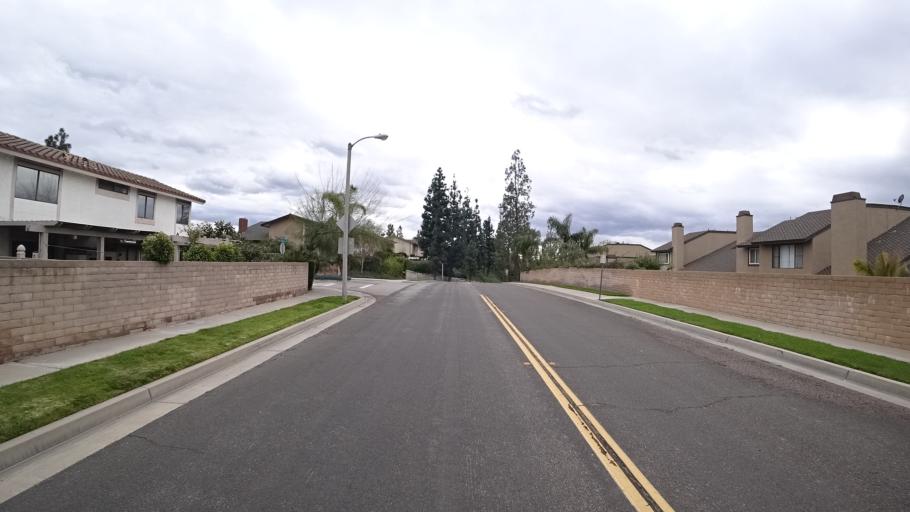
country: US
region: California
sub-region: Orange County
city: Yorba Linda
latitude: 33.8716
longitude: -117.8196
